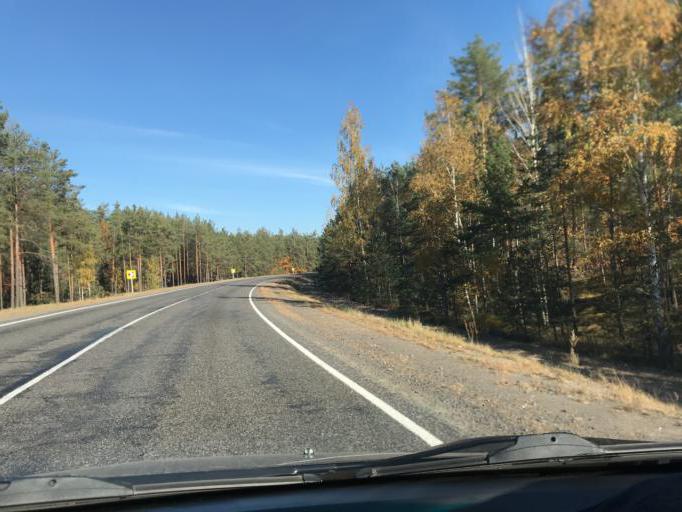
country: BY
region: Gomel
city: Sasnovy Bor
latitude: 52.5319
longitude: 29.3290
